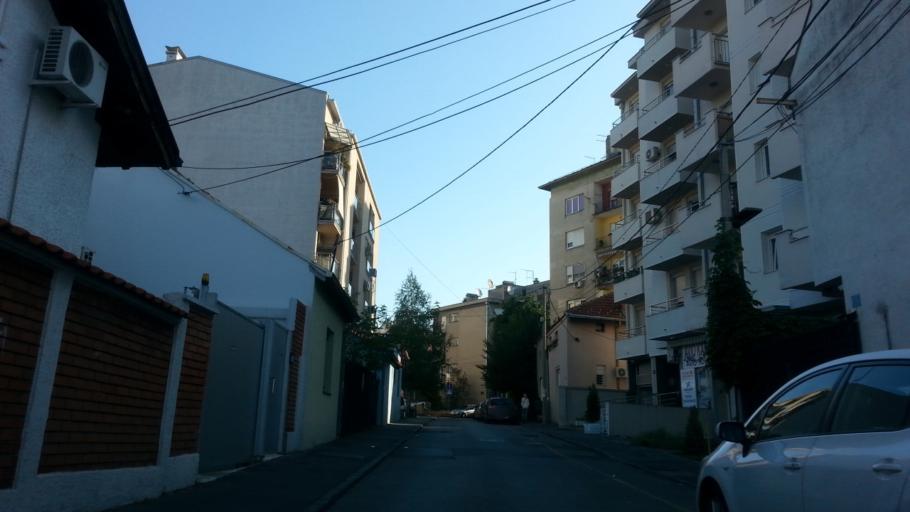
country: RS
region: Central Serbia
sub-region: Belgrade
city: Vracar
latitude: 44.7957
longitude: 20.4902
